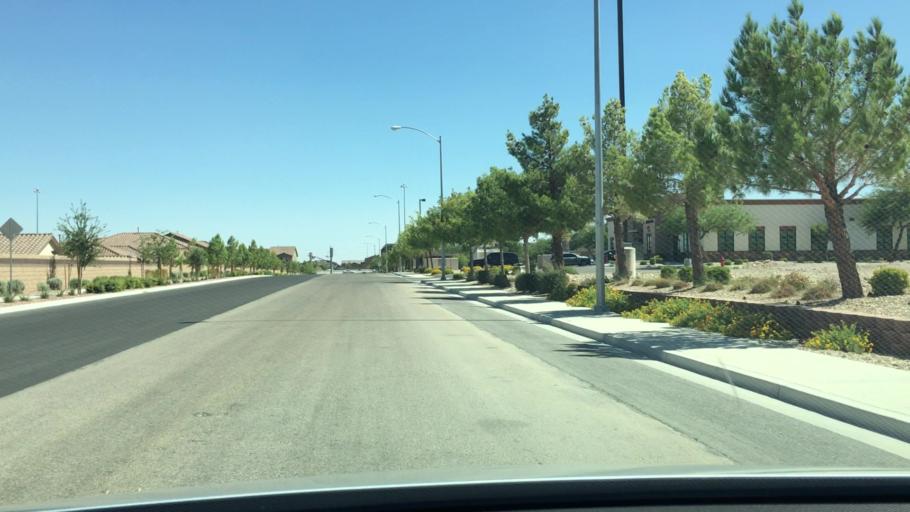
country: US
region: Nevada
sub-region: Clark County
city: Summerlin South
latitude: 36.0759
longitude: -115.2927
